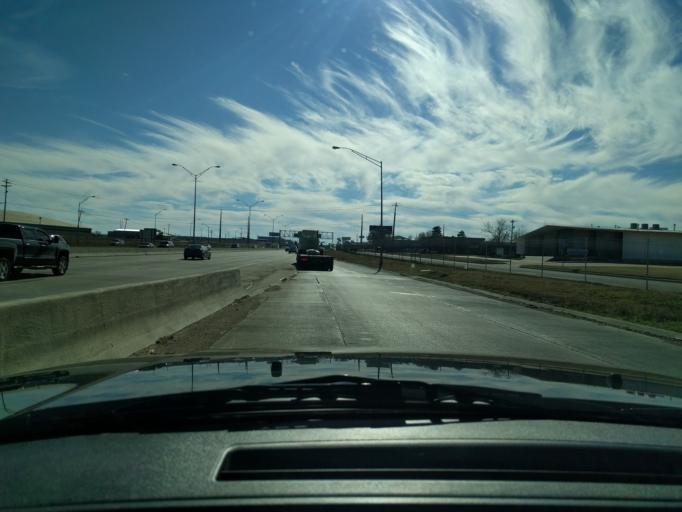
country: US
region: Oklahoma
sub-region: Cleveland County
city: Moore
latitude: 35.3893
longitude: -97.4953
